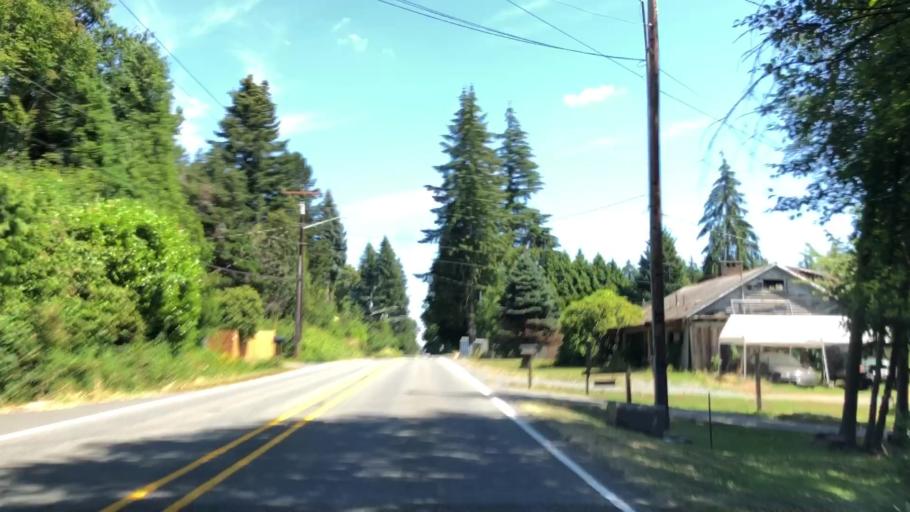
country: US
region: Washington
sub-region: Snohomish County
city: Clearview
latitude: 47.8341
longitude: -122.1444
